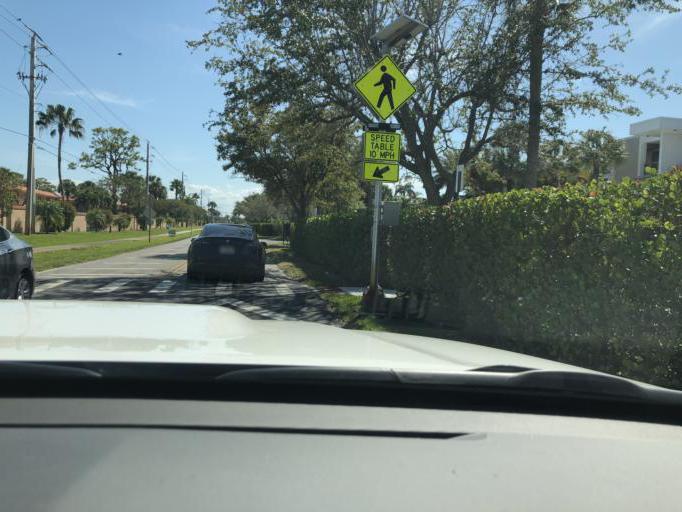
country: US
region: Florida
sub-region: Martin County
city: Palm City
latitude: 27.1792
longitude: -80.2571
